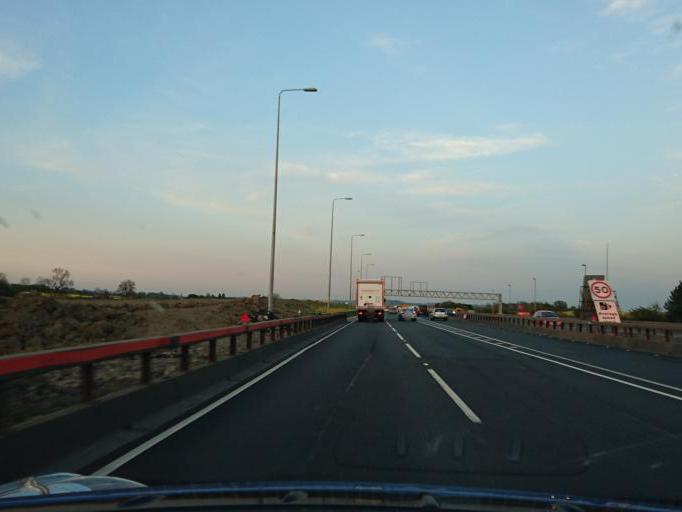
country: GB
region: England
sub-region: Leicestershire
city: Lutterworth
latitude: 52.4054
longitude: -1.1924
